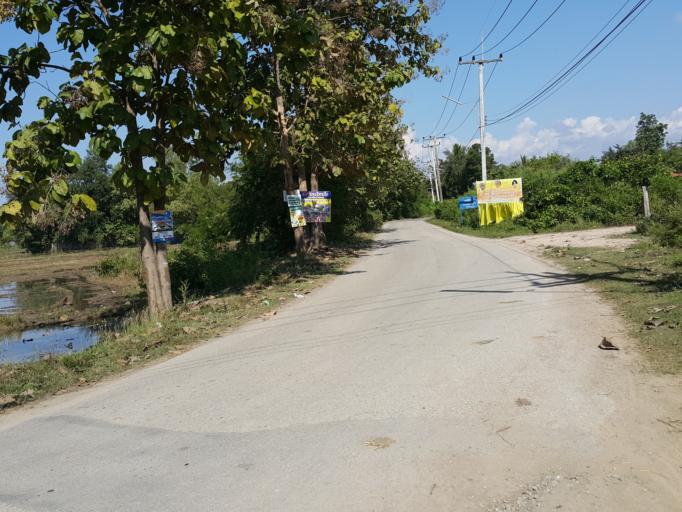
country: TH
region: Chiang Mai
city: San Kamphaeng
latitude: 18.7758
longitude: 99.1276
